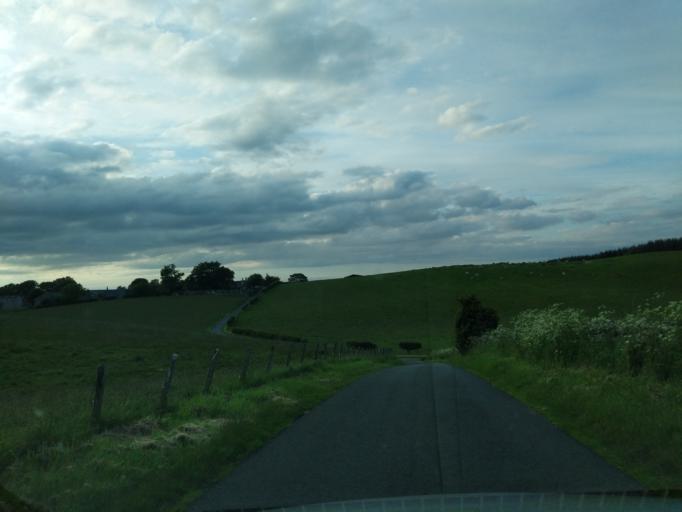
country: GB
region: Scotland
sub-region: Midlothian
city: Gorebridge
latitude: 55.7948
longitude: -3.0918
